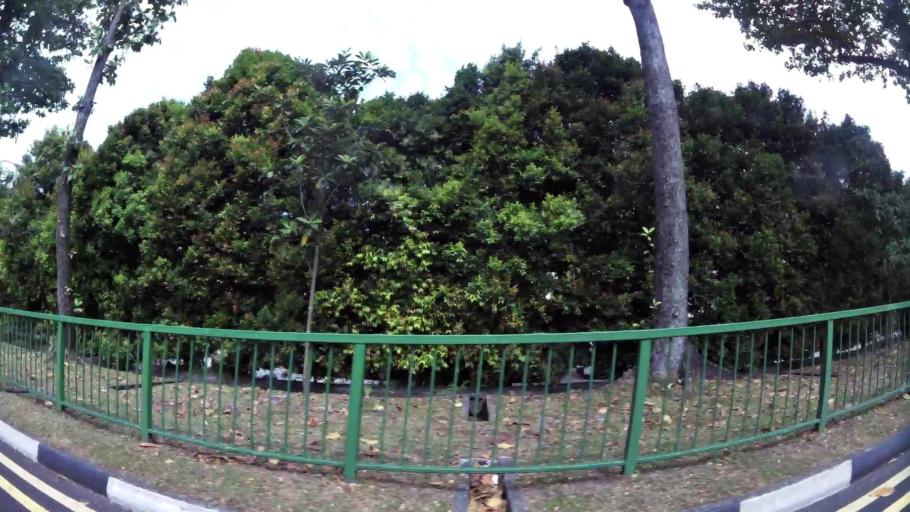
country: SG
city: Singapore
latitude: 1.3071
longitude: 103.7639
